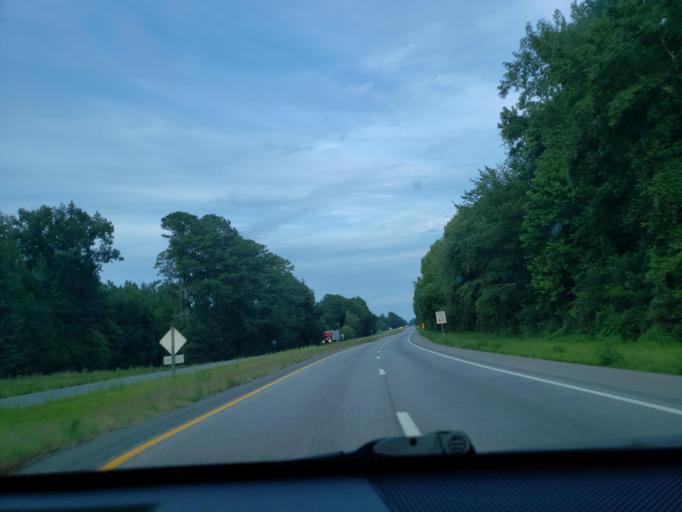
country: US
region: Virginia
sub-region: Sussex County
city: Sussex
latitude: 36.7072
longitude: -77.3025
